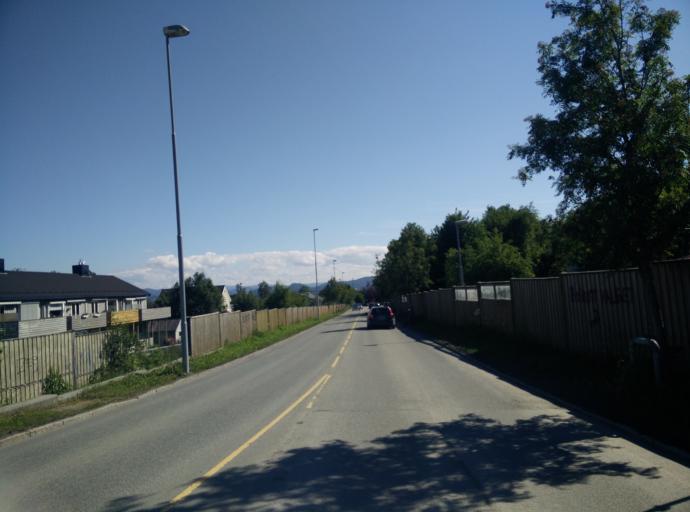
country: NO
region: Sor-Trondelag
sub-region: Trondheim
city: Trondheim
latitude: 63.4012
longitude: 10.3574
